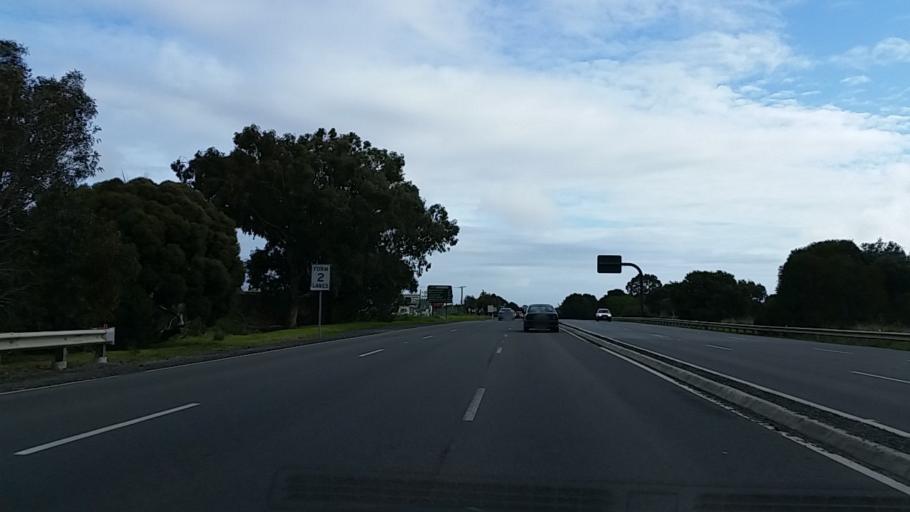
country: AU
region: South Australia
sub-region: Marion
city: Trott Park
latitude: -35.0831
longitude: 138.5452
